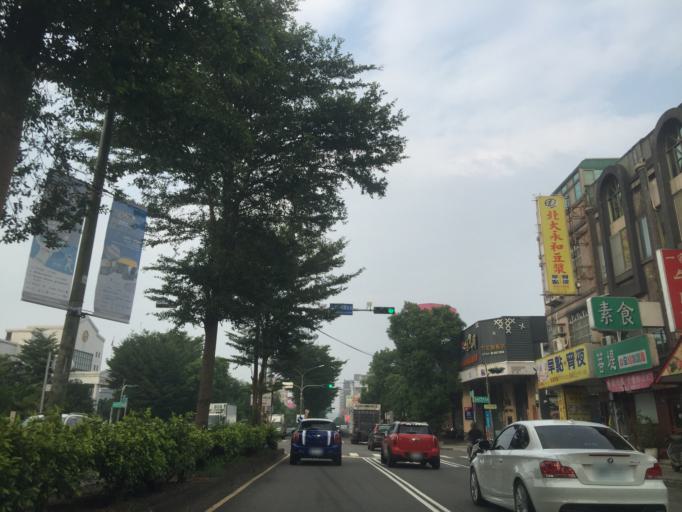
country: TW
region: Taiwan
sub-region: Hsinchu
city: Zhubei
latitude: 24.8266
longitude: 121.0159
